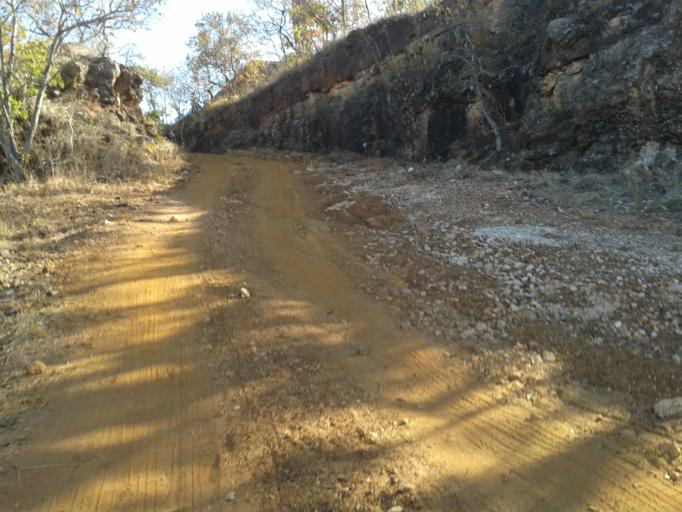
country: BR
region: Minas Gerais
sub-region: Capinopolis
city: Capinopolis
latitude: -18.7612
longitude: -49.5383
